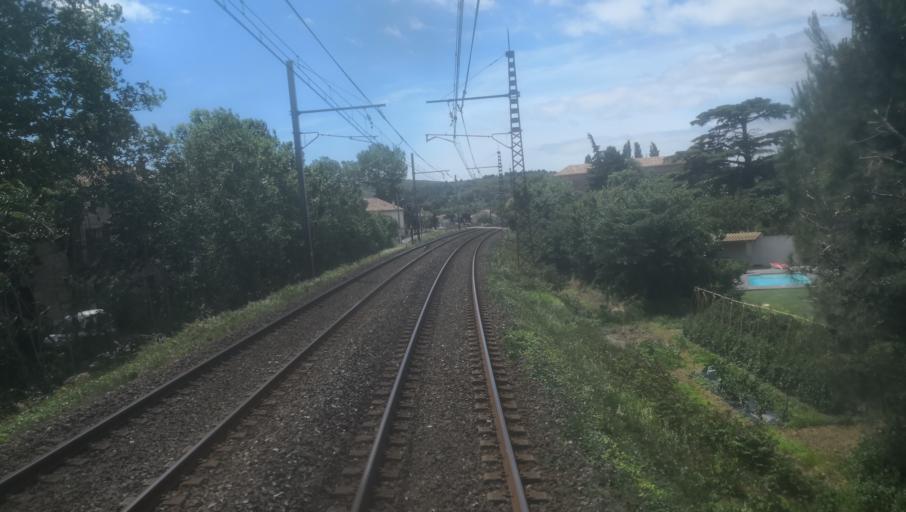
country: FR
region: Languedoc-Roussillon
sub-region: Departement de l'Aude
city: Nevian
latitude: 43.2104
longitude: 2.9059
